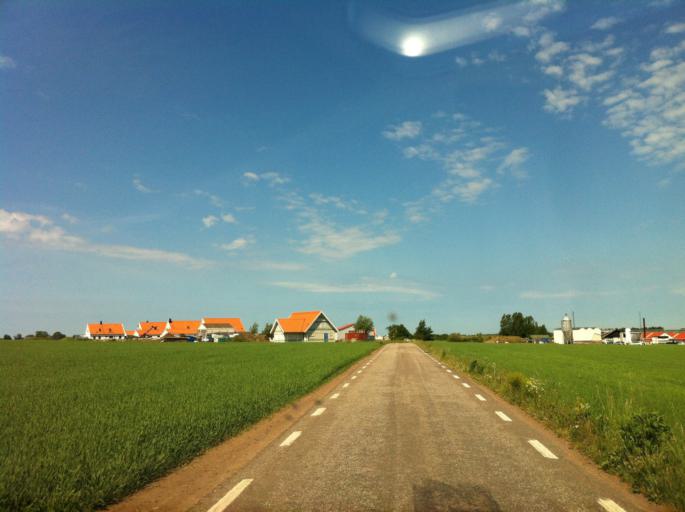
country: SE
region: Skane
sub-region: Helsingborg
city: Glumslov
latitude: 55.9443
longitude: 12.8810
